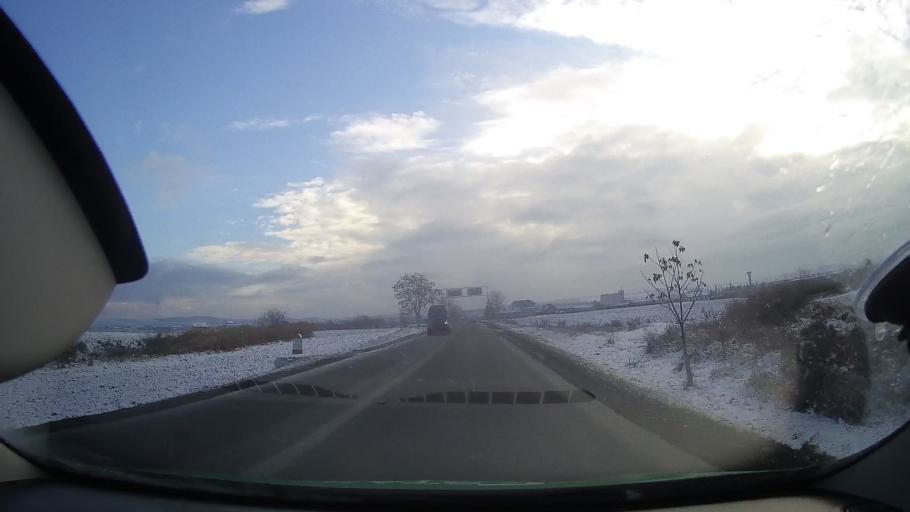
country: RO
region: Mures
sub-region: Comuna Iernut
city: Iernut
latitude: 46.4433
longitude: 24.2516
